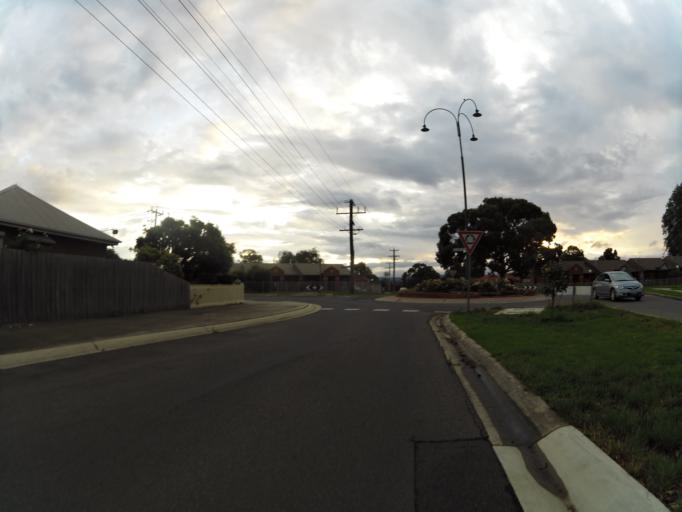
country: AU
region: Victoria
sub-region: Latrobe
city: Morwell
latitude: -38.2378
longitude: 146.3898
